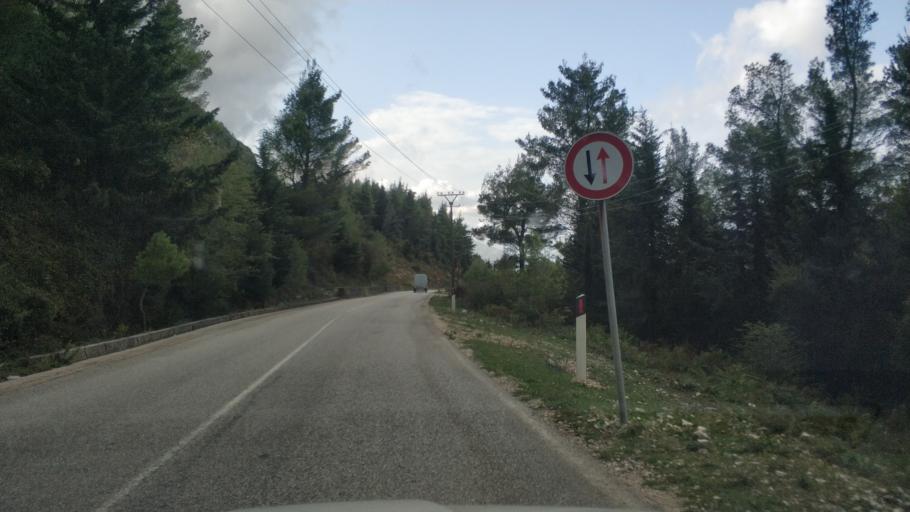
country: AL
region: Vlore
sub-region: Rrethi i Vlores
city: Orikum
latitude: 40.2570
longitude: 19.5287
